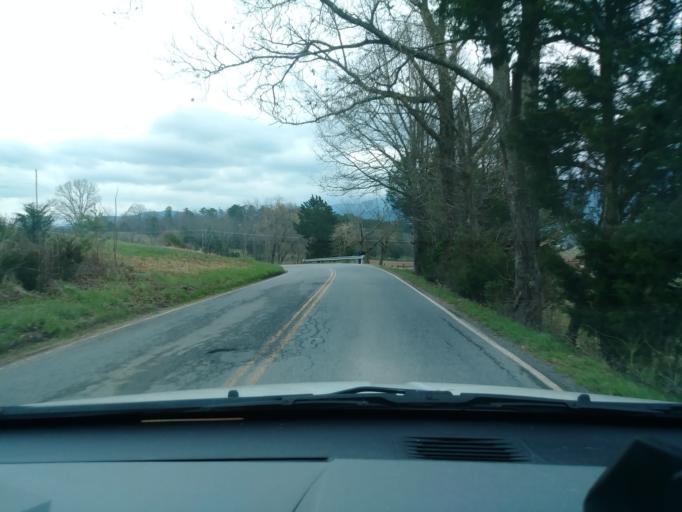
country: US
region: Tennessee
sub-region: Greene County
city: Tusculum
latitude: 36.0928
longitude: -82.7592
